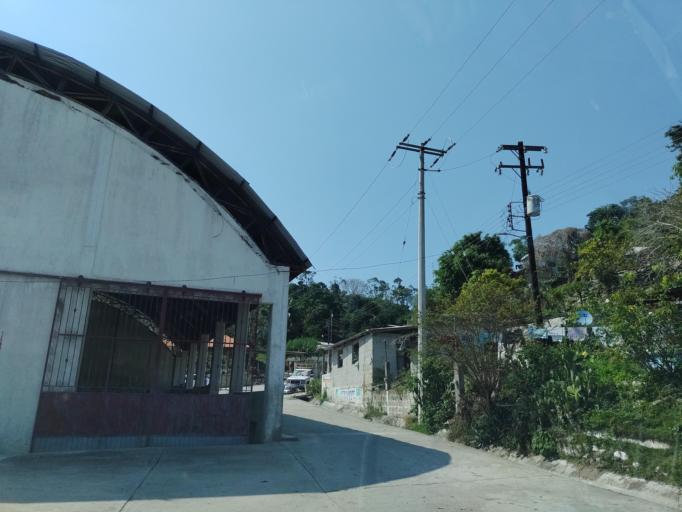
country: MX
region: Veracruz
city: Agua Dulce
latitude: 20.3367
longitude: -97.2030
